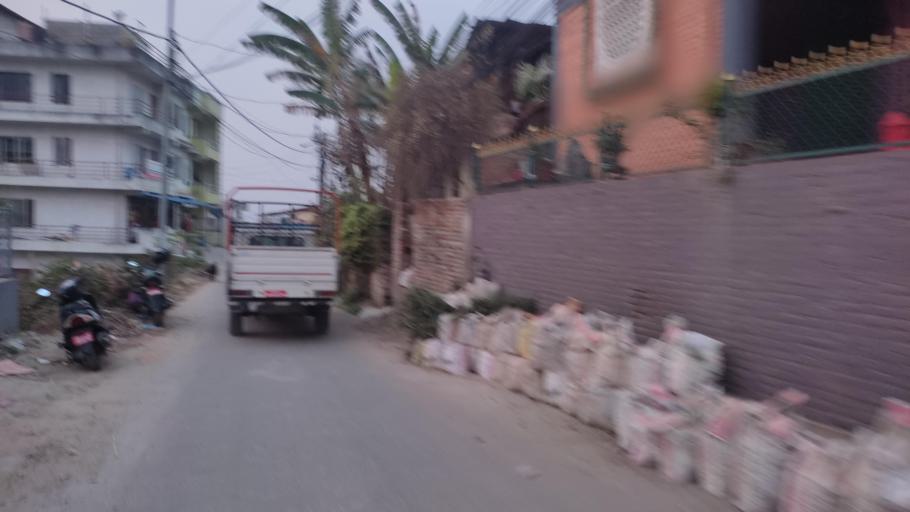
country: NP
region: Central Region
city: Kirtipur
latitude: 27.6681
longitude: 85.2868
